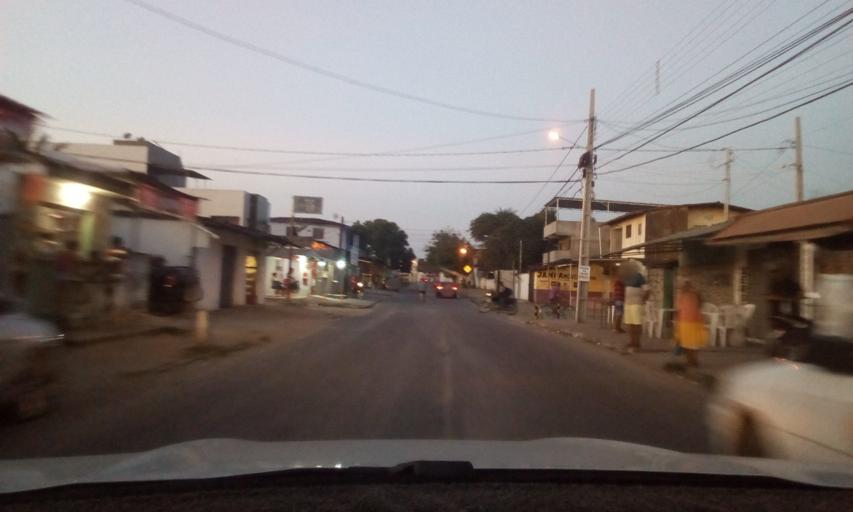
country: BR
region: Paraiba
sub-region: Bayeux
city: Bayeux
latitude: -7.1634
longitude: -34.9066
